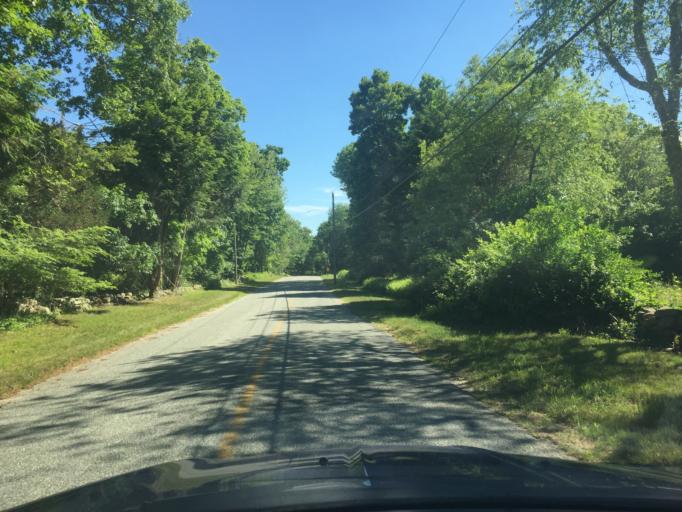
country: US
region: Rhode Island
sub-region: Washington County
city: Hopkinton
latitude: 41.4893
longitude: -71.8095
